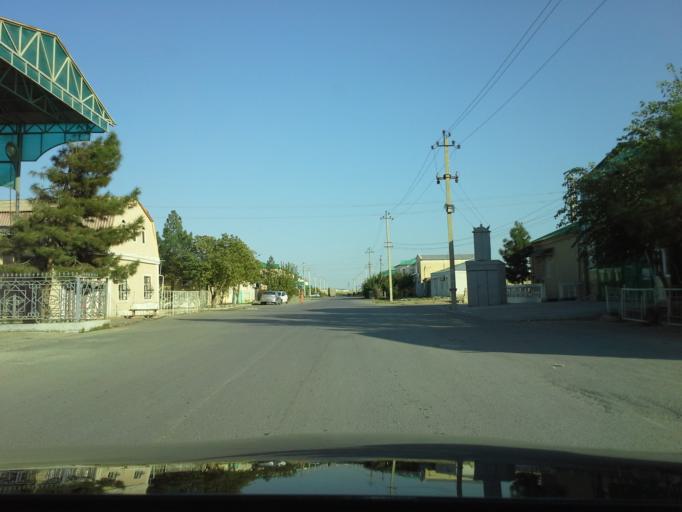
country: TM
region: Ahal
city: Abadan
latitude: 38.0486
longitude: 58.1678
